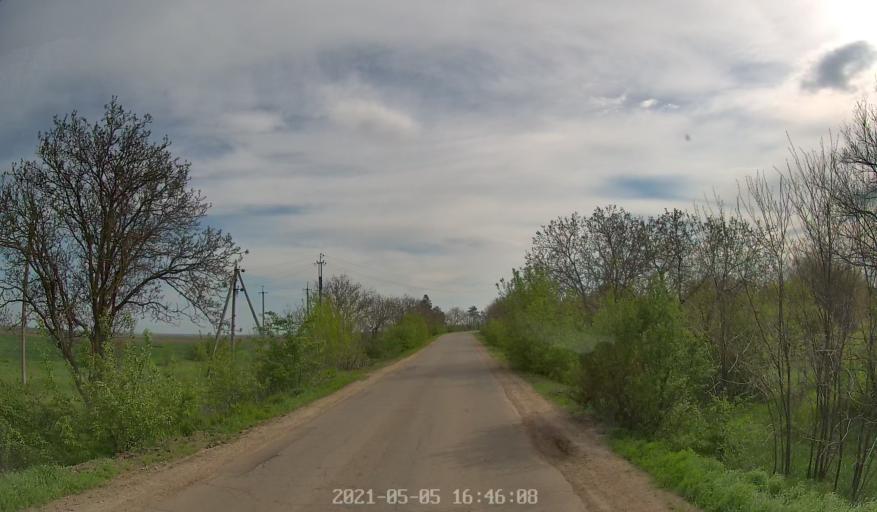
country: MD
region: Criuleni
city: Criuleni
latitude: 47.1030
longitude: 29.1922
